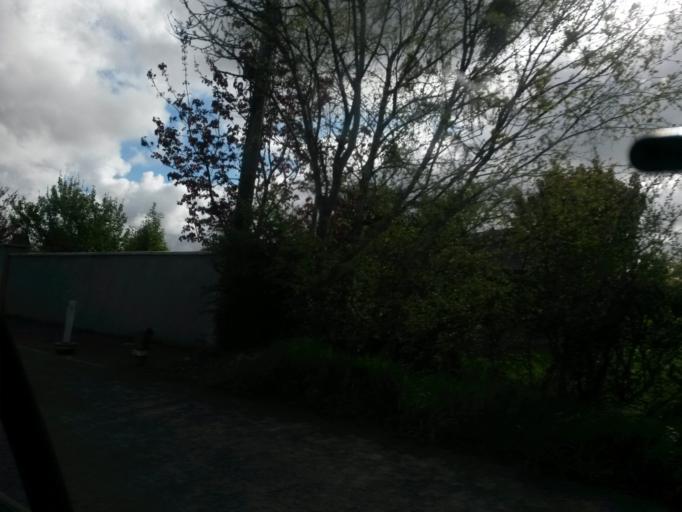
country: IE
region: Leinster
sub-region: Loch Garman
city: Ferns
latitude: 52.5744
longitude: -6.5171
